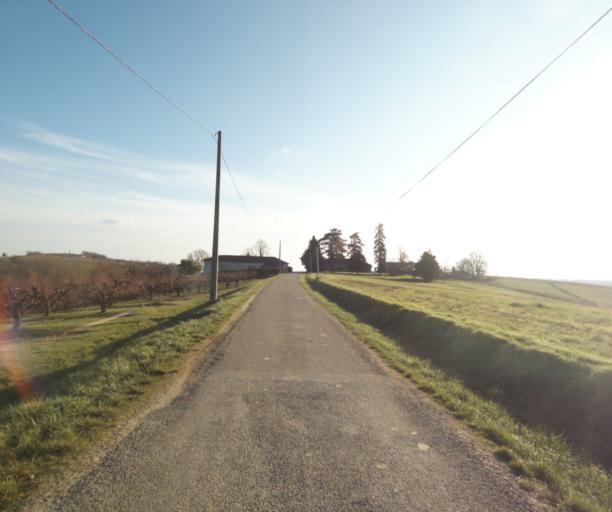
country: FR
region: Midi-Pyrenees
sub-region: Departement du Tarn-et-Garonne
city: Moissac
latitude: 44.1365
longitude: 1.1112
